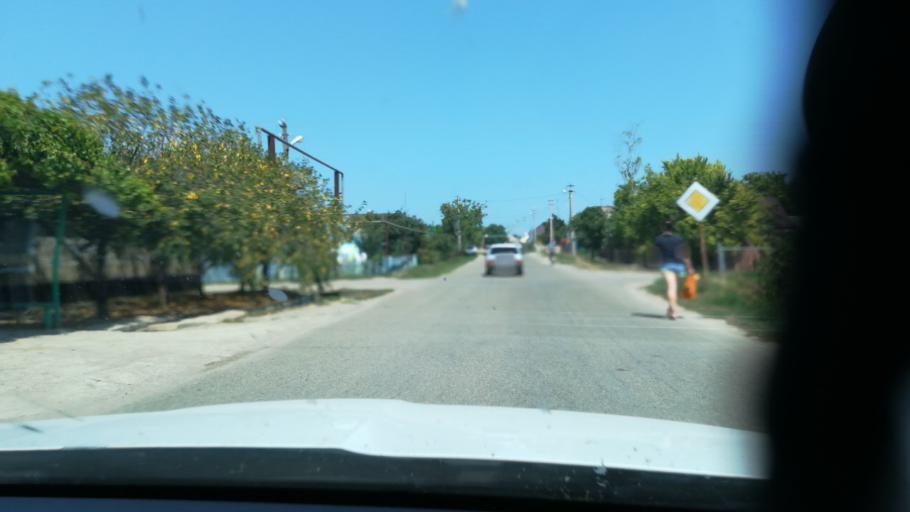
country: RU
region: Krasnodarskiy
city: Starotitarovskaya
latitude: 45.2114
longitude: 37.1447
